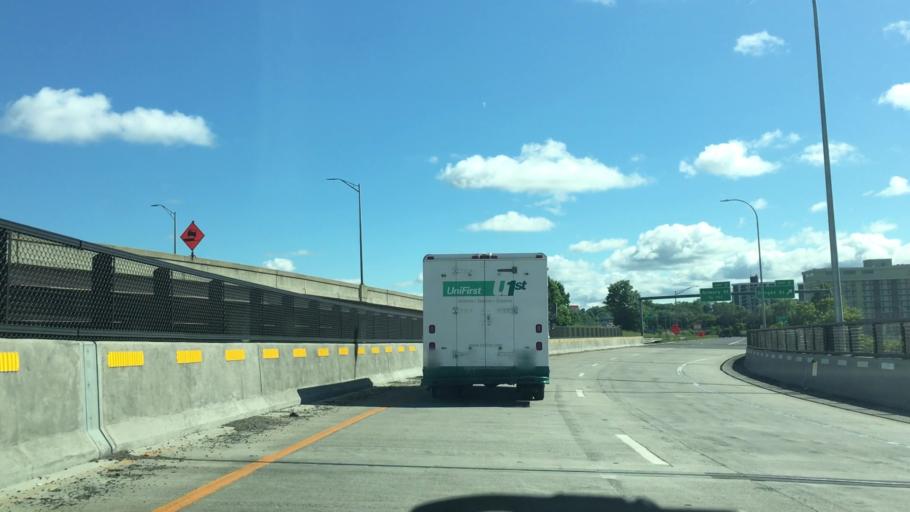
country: US
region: Massachusetts
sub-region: Hampden County
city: Springfield
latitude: 42.1075
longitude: -72.6000
